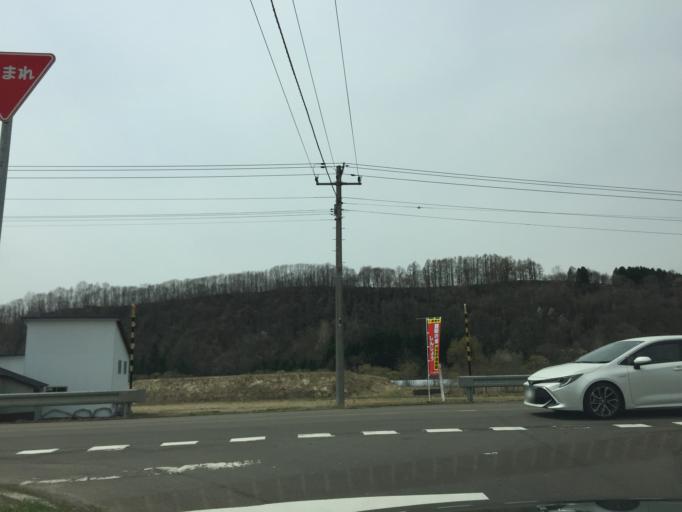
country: JP
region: Hokkaido
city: Ashibetsu
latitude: 43.6071
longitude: 142.2047
